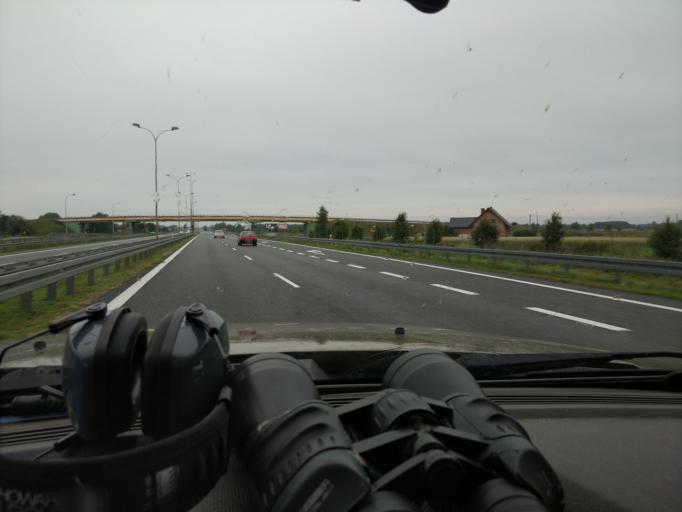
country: PL
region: Masovian Voivodeship
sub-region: Powiat wolominski
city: Dabrowka
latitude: 52.4799
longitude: 21.3419
